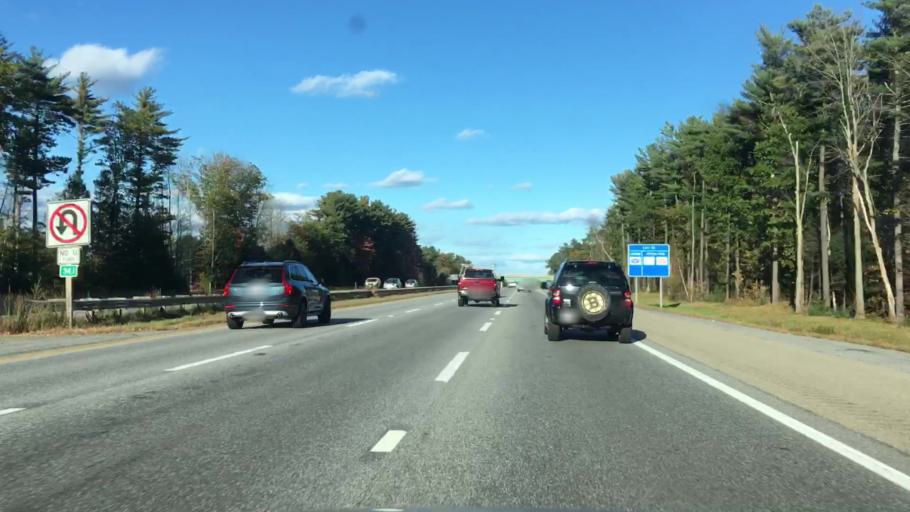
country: US
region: Maine
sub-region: York County
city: Biddeford
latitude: 43.5110
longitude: -70.4745
